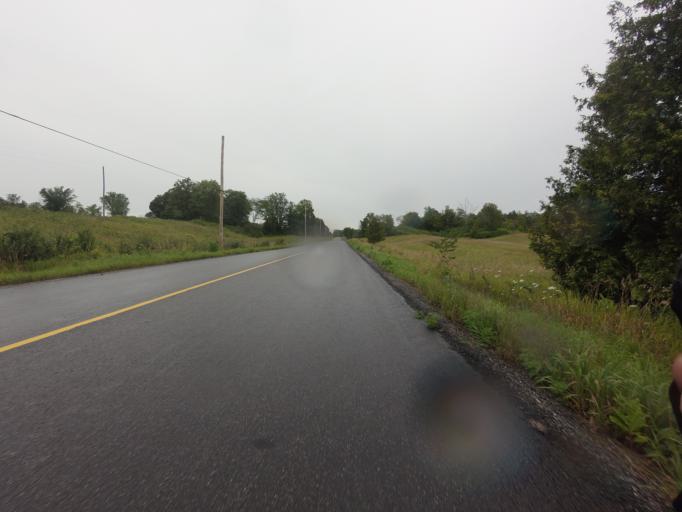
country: CA
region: Ontario
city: Perth
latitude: 44.9409
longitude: -76.4343
